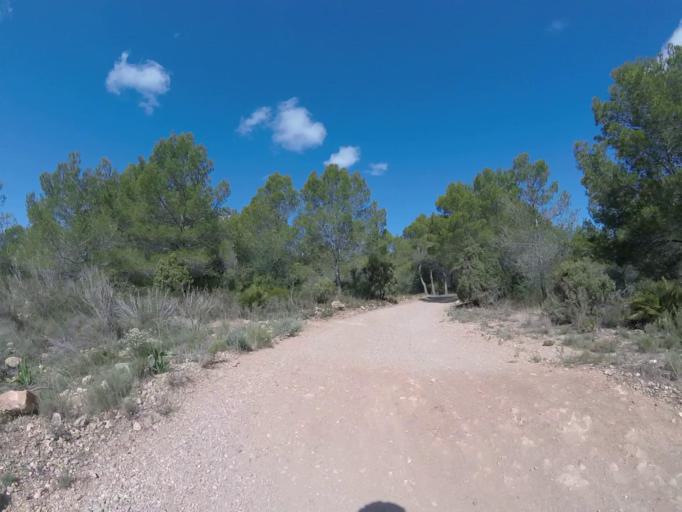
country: ES
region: Valencia
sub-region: Provincia de Castello
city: Alcoceber
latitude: 40.2911
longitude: 0.3159
